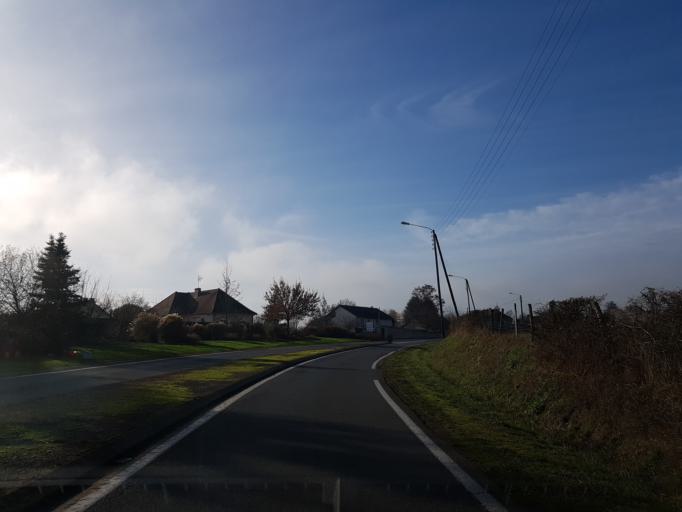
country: FR
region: Bourgogne
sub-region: Departement de Saone-et-Loire
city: Gueugnon
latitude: 46.5959
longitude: 4.0443
